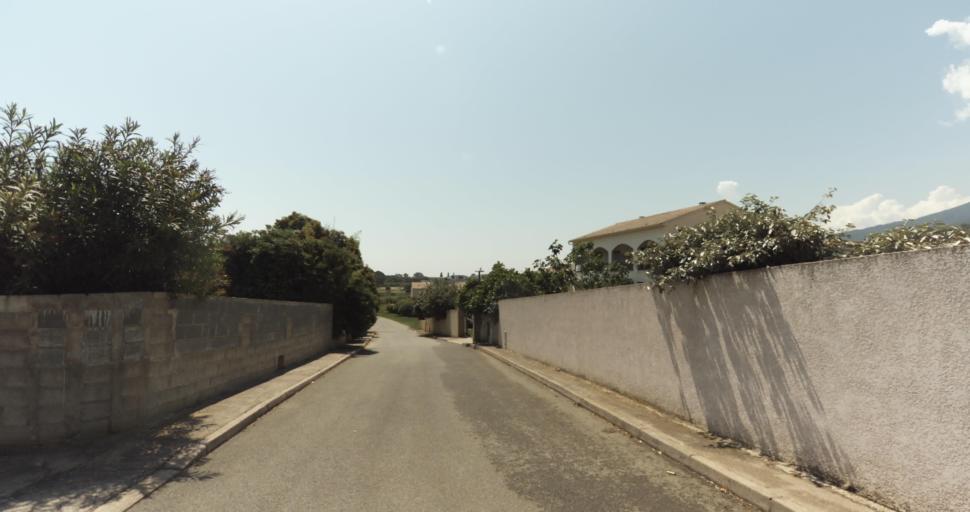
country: FR
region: Corsica
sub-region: Departement de la Haute-Corse
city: Biguglia
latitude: 42.6041
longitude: 9.4319
